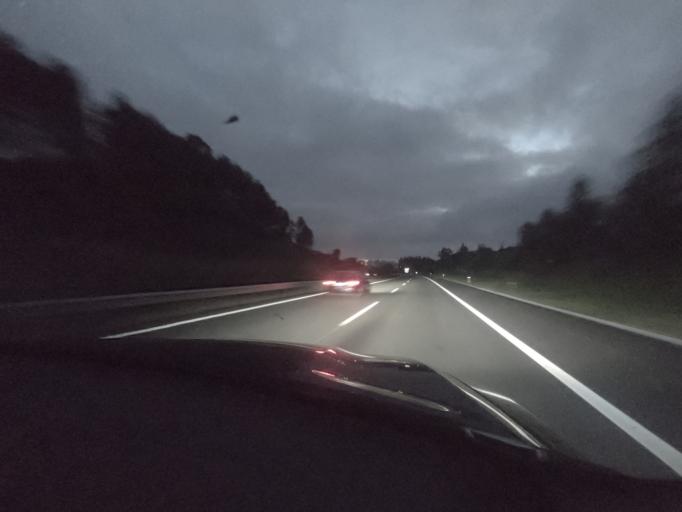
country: PT
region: Leiria
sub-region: Leiria
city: Caranguejeira
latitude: 39.7780
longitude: -8.7408
